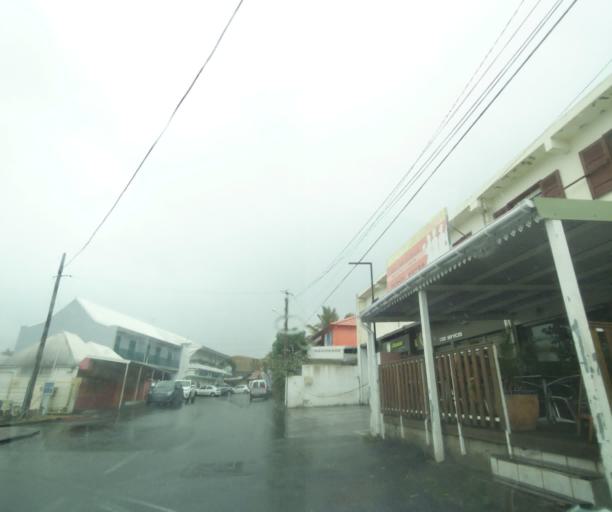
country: RE
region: Reunion
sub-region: Reunion
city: La Possession
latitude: -20.9830
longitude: 55.3265
